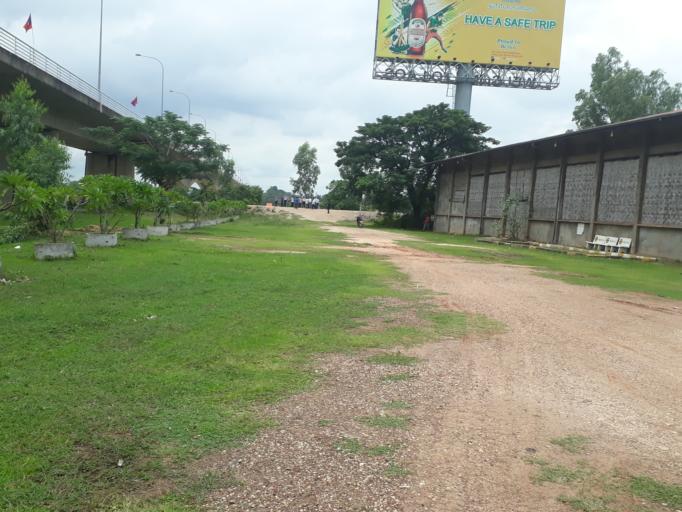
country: TH
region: Nong Khai
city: Nong Khai
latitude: 17.8841
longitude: 102.7143
